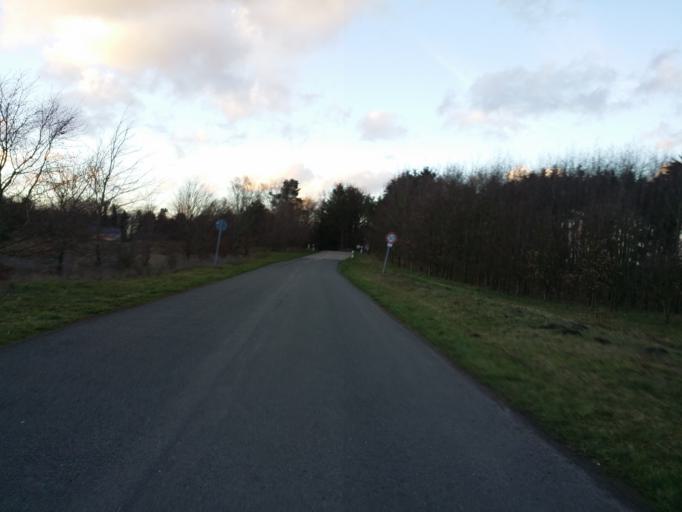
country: DE
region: Lower Saxony
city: Gross Ippener
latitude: 52.9726
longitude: 8.5979
